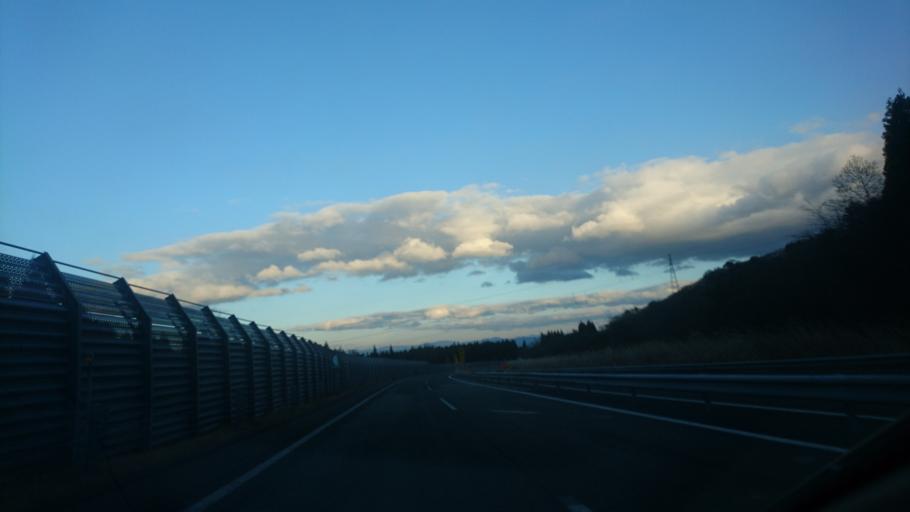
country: JP
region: Iwate
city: Kitakami
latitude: 39.2957
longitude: 140.9614
